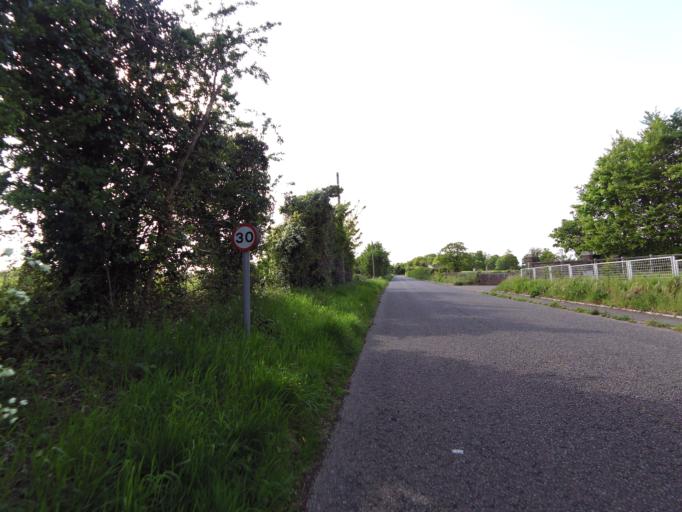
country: GB
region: England
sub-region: Suffolk
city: Beccles
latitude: 52.4482
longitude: 1.6125
